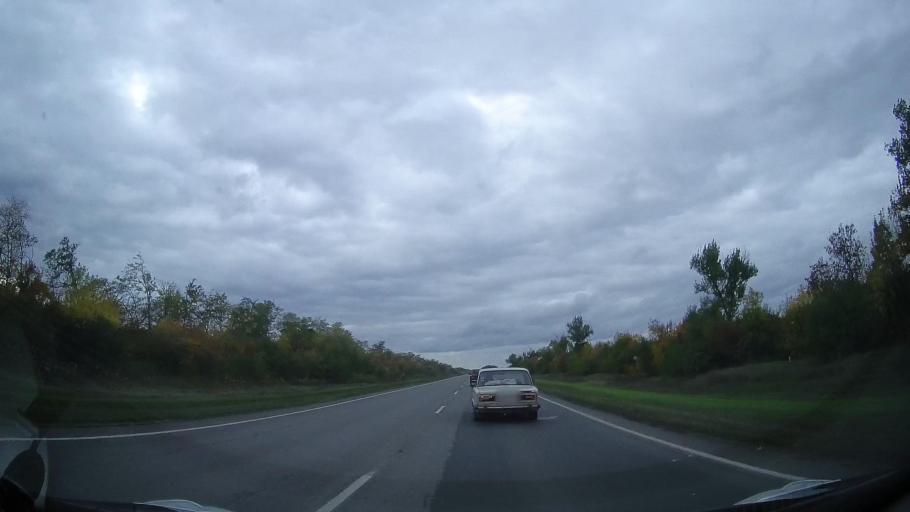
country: RU
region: Rostov
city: Yegorlykskaya
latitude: 46.5474
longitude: 40.7500
